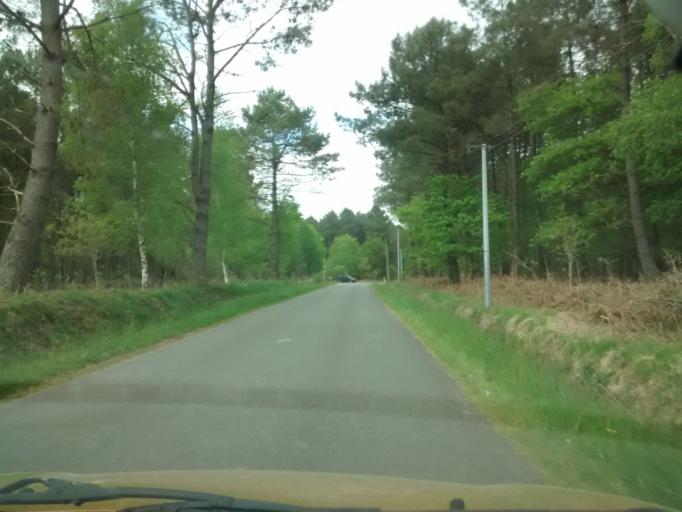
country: FR
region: Brittany
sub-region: Departement du Morbihan
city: Molac
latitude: 47.7359
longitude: -2.4214
